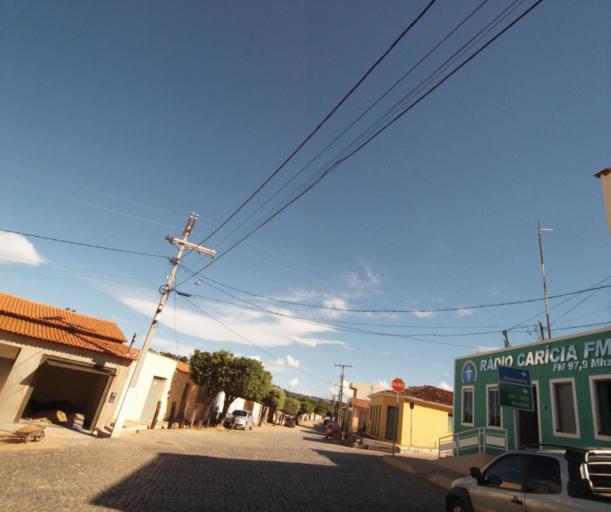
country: BR
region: Bahia
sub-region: Correntina
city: Correntina
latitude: -13.3432
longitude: -44.6360
